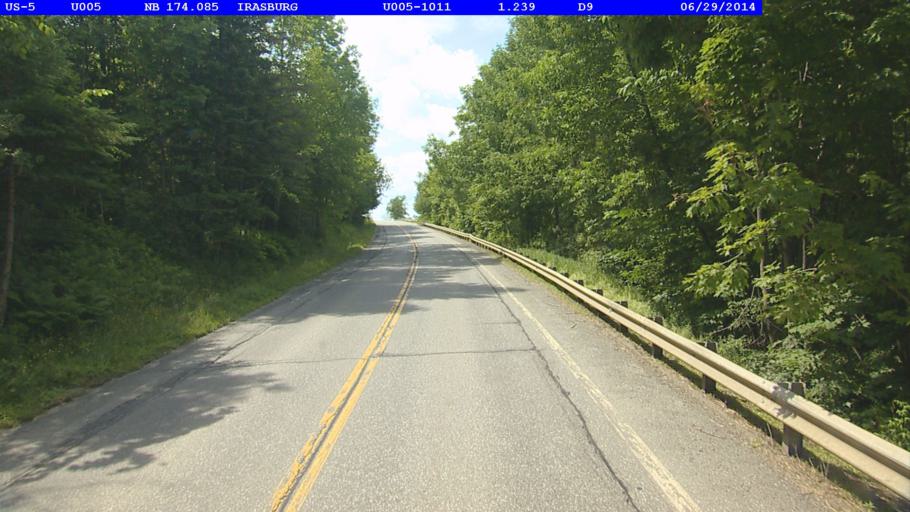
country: US
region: Vermont
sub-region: Orleans County
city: Newport
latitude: 44.8219
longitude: -72.2266
